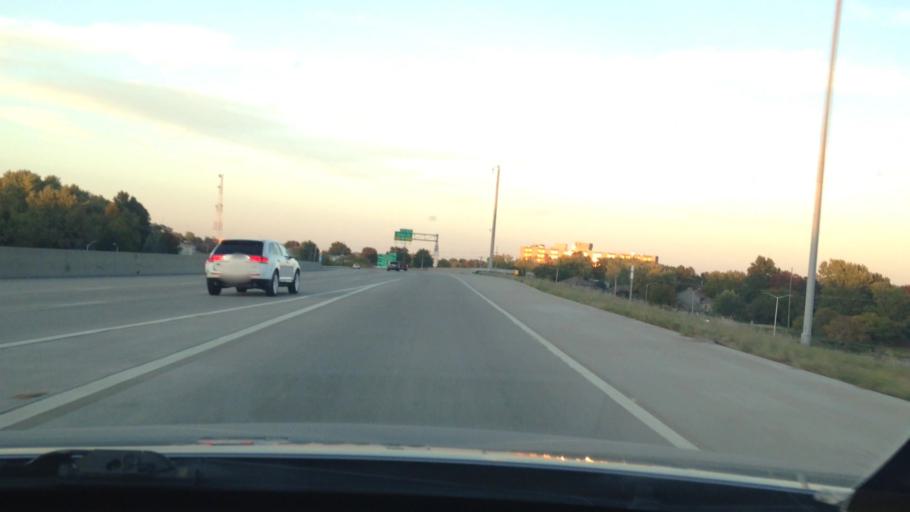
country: US
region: Kansas
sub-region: Johnson County
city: Olathe
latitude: 38.8711
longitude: -94.7961
